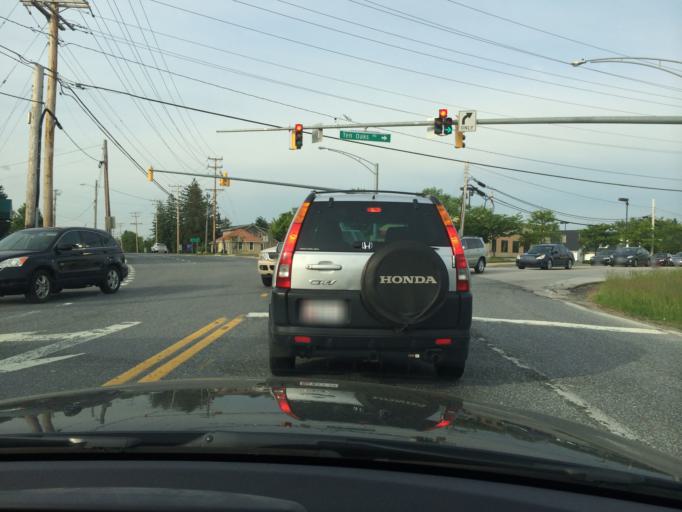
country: US
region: Maryland
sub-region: Howard County
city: Highland
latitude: 39.2068
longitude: -76.9427
